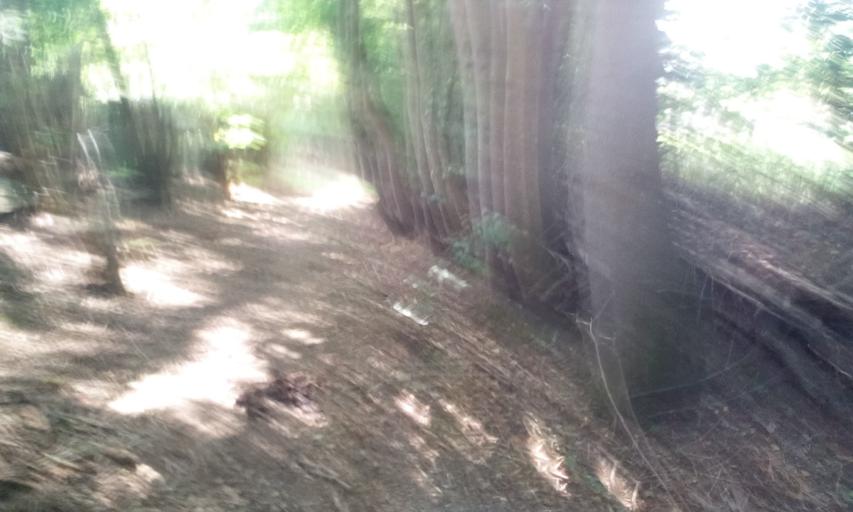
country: FR
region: Lower Normandy
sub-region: Departement du Calvados
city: Argences
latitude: 49.1269
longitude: -0.1572
